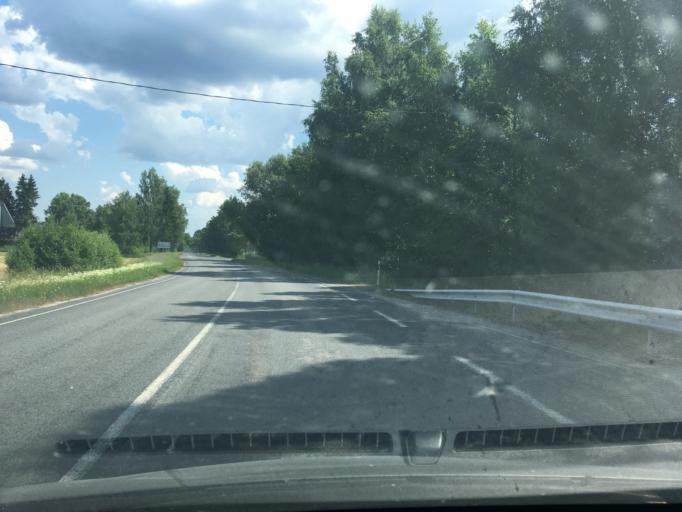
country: EE
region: Paernumaa
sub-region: Halinga vald
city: Parnu-Jaagupi
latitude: 58.7124
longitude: 24.3683
